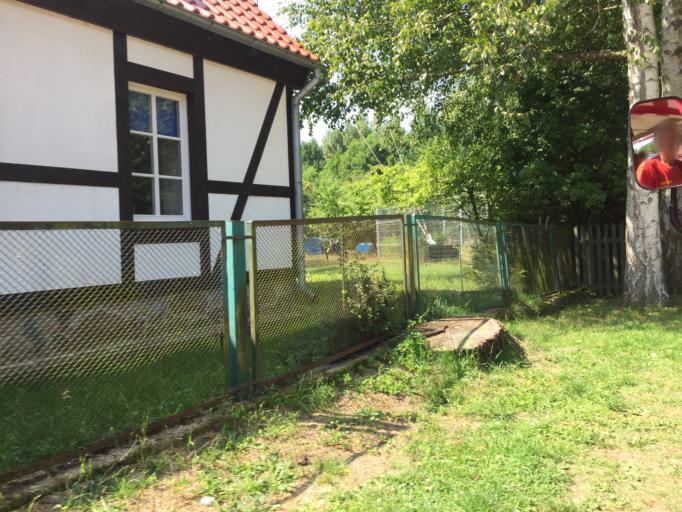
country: PL
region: Pomeranian Voivodeship
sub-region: Powiat leborski
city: Leba
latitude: 54.7543
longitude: 17.5143
